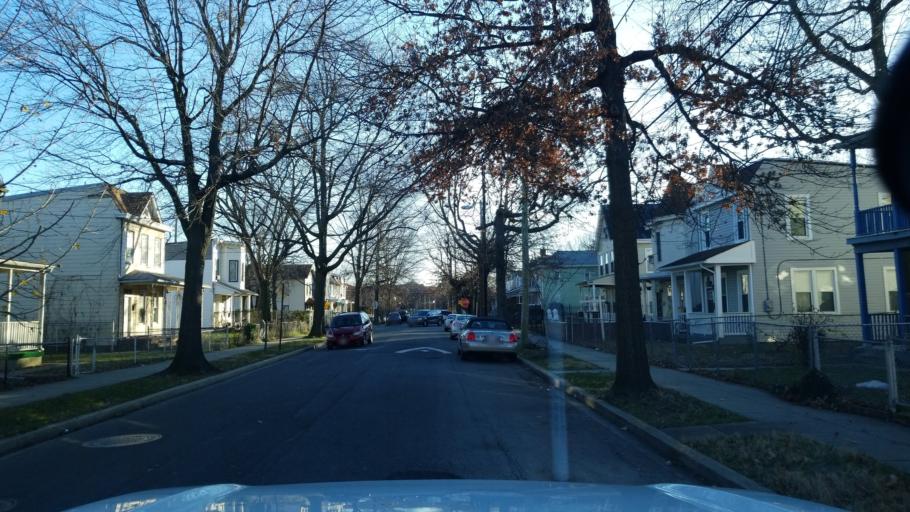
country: US
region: Maryland
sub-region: Prince George's County
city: Glassmanor
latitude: 38.8451
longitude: -76.9956
